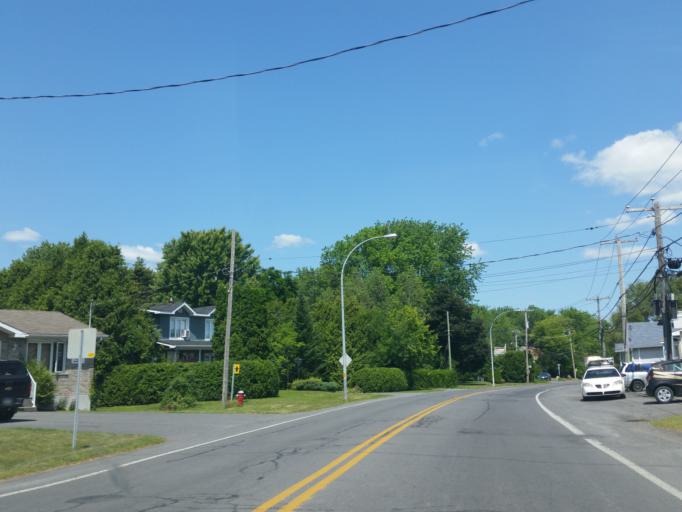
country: CA
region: Quebec
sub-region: Monteregie
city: Saint-Jean-sur-Richelieu
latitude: 45.3498
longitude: -73.2664
